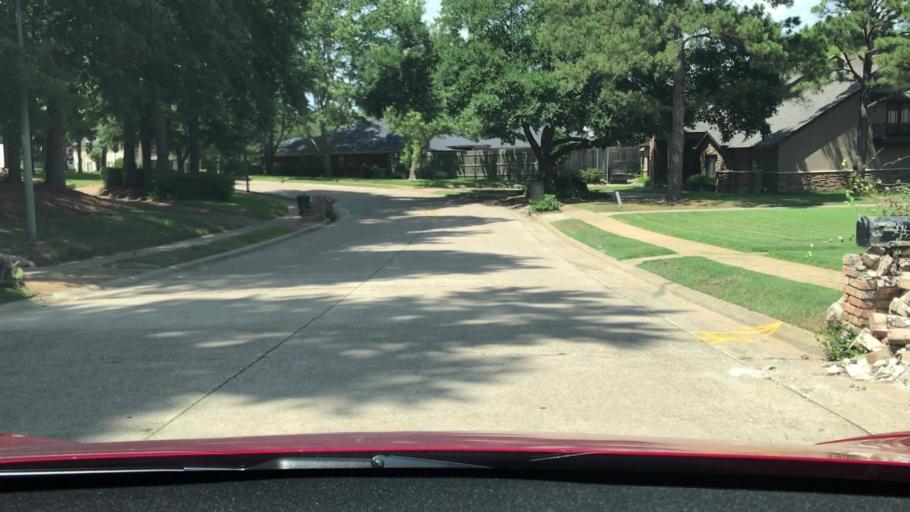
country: US
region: Louisiana
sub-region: Bossier Parish
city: Bossier City
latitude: 32.4242
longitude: -93.7286
